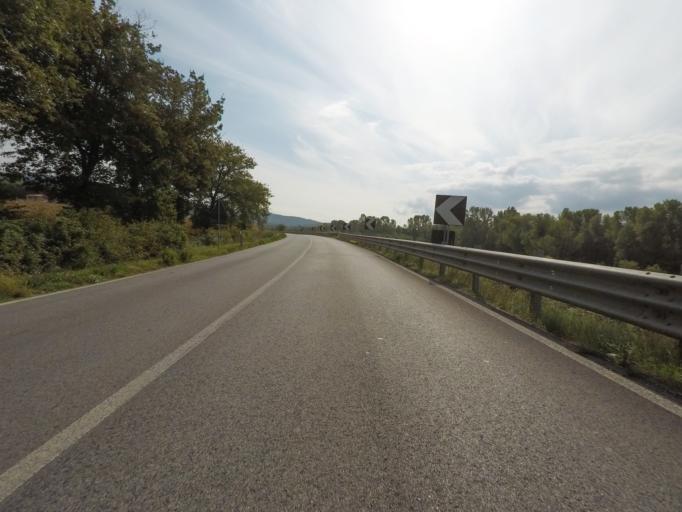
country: IT
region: Tuscany
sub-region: Provincia di Siena
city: Rosia
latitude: 43.1723
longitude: 11.2808
